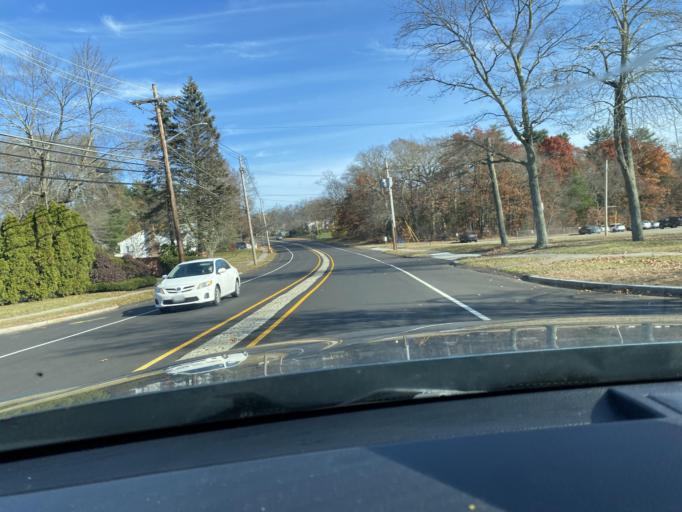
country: US
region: Massachusetts
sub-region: Norfolk County
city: Norwood
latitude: 42.1848
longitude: -71.2213
